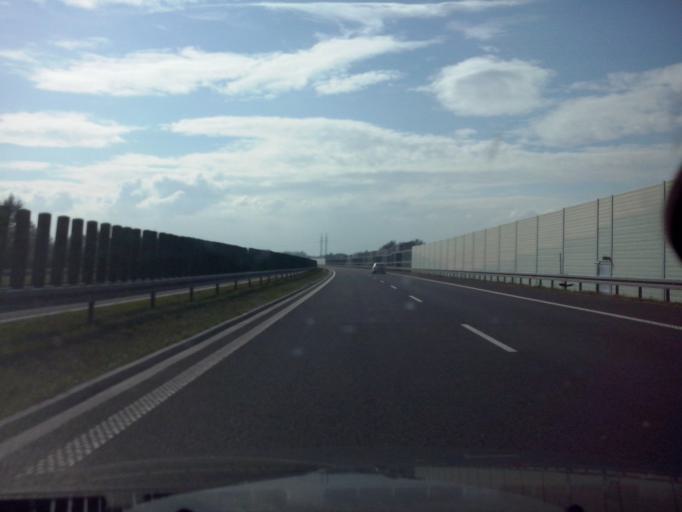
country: PL
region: Lesser Poland Voivodeship
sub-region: Powiat tarnowski
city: Lukowa
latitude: 50.0582
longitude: 20.9330
